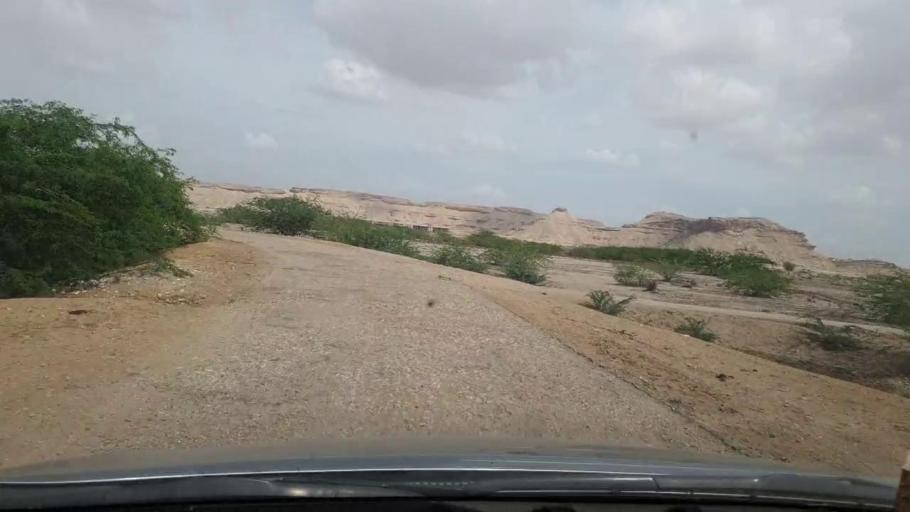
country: PK
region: Sindh
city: Khairpur
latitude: 27.4722
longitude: 68.8529
